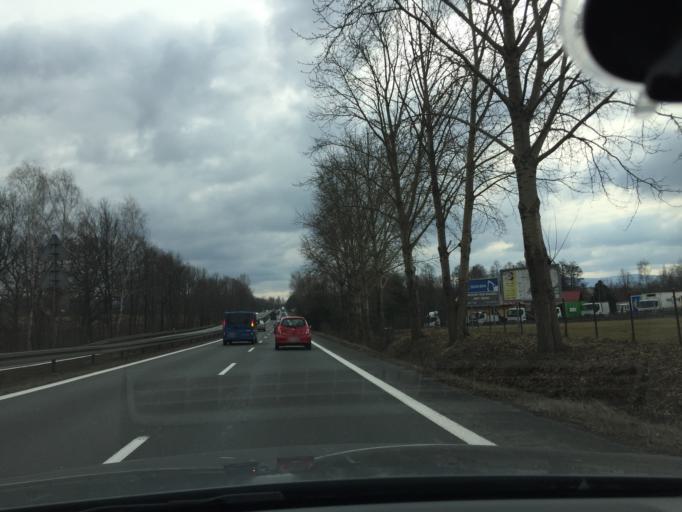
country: PL
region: Silesian Voivodeship
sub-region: Powiat bielski
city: Czechowice-Dziedzice
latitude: 49.8900
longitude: 18.9951
